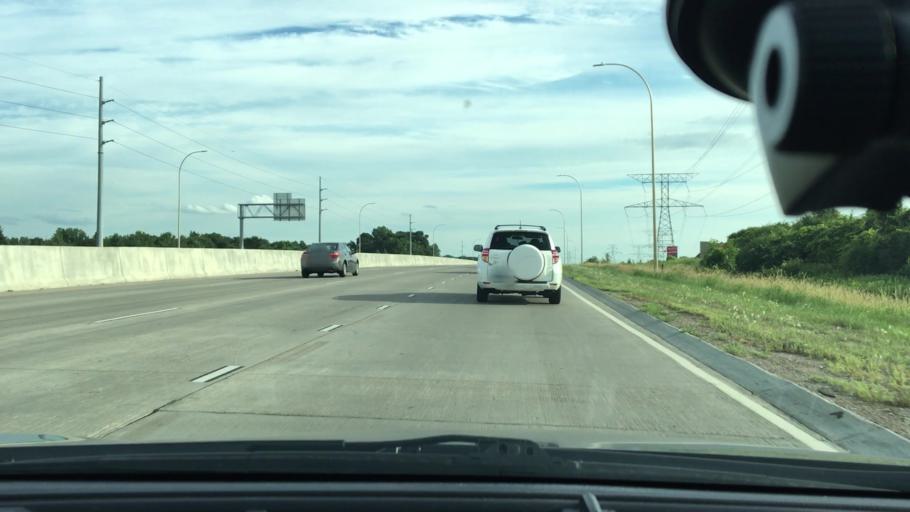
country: US
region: Minnesota
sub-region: Hennepin County
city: Plymouth
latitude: 45.0259
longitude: -93.4533
